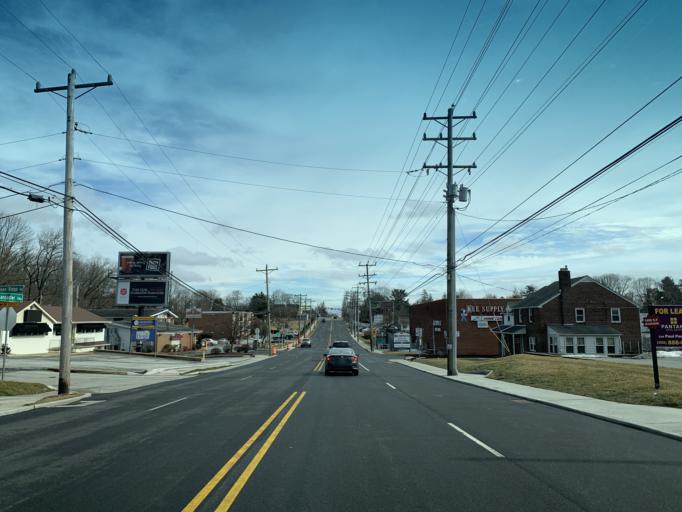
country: US
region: Delaware
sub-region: New Castle County
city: Elsmere
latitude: 39.7547
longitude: -75.5942
